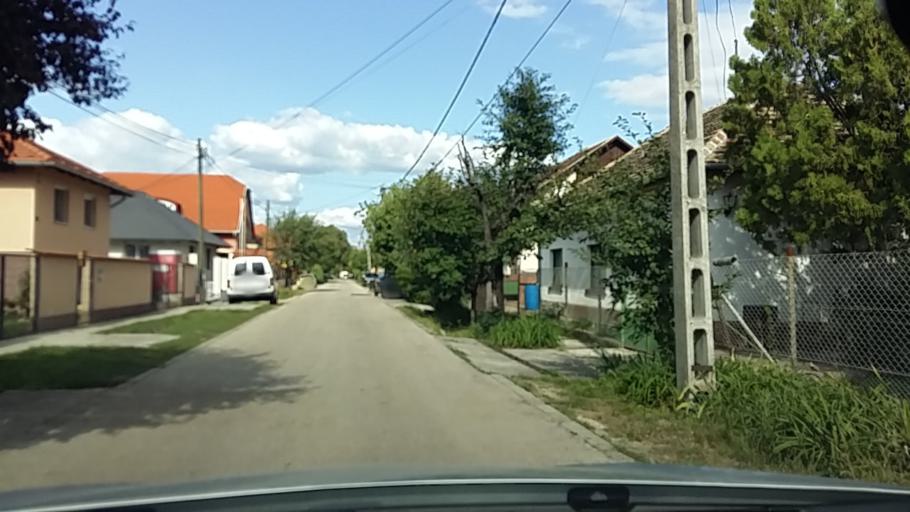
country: HU
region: Pest
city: Vecses
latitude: 47.4080
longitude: 19.2618
